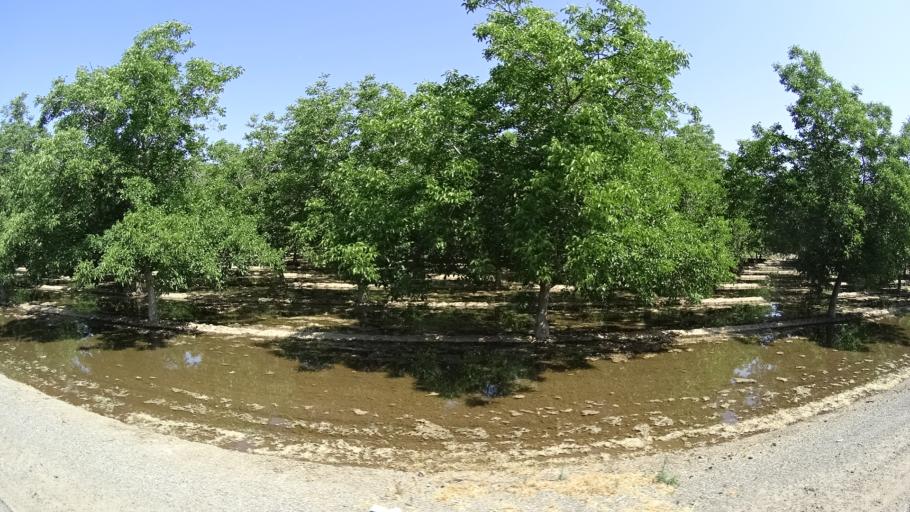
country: US
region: California
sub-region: Kings County
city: Lucerne
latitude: 36.3717
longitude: -119.6782
